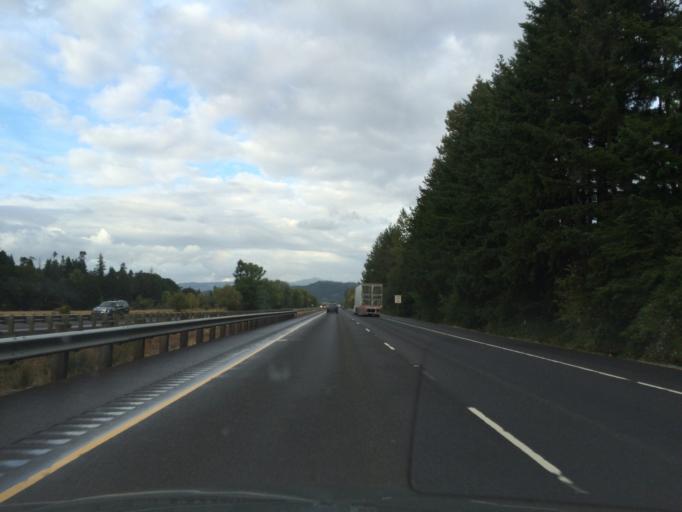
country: US
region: Oregon
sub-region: Lane County
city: Cottage Grove
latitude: 43.7519
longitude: -123.1076
